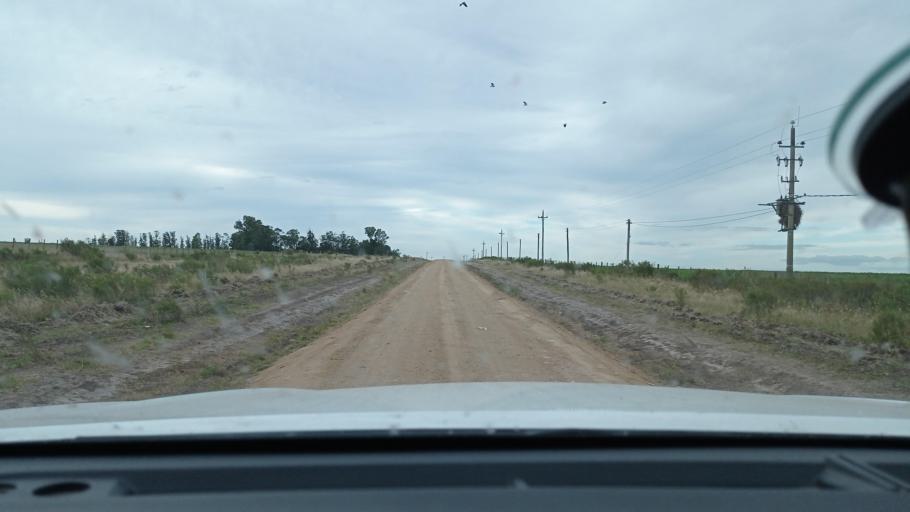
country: UY
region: Florida
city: Casupa
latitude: -34.1146
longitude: -55.7676
